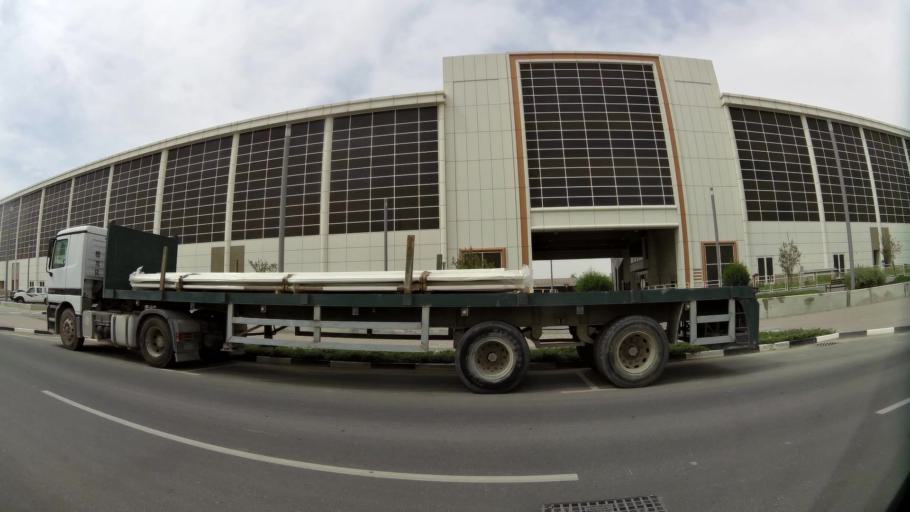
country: QA
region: Al Wakrah
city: Al Wukayr
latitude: 25.1982
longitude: 51.4525
